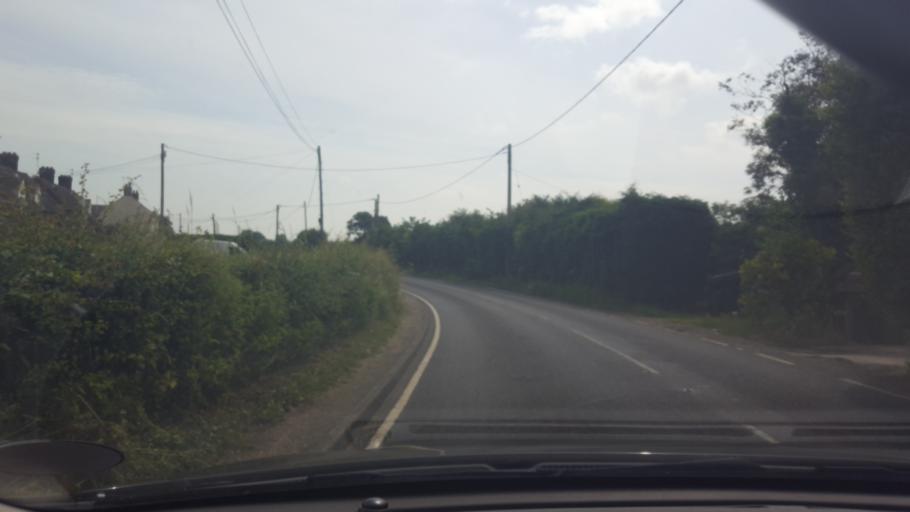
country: GB
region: England
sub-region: Essex
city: Great Bentley
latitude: 51.8836
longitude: 1.1108
